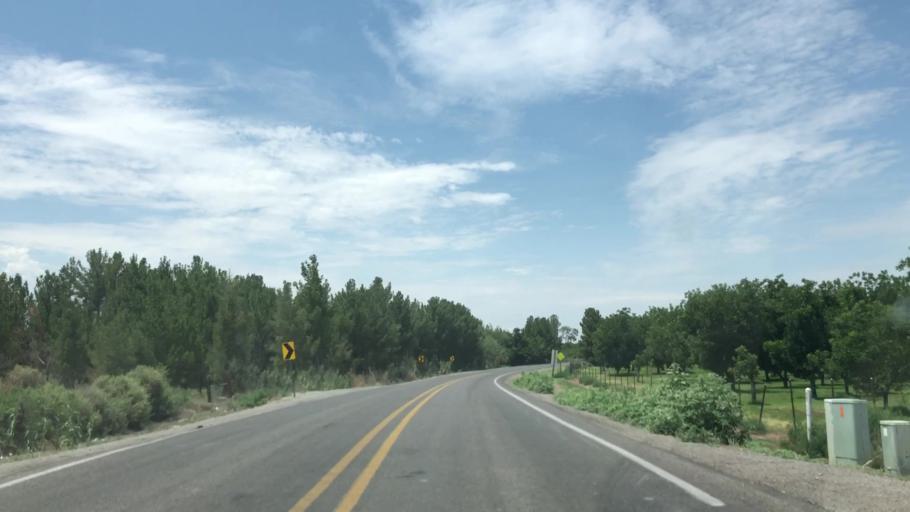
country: US
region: New Mexico
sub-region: Dona Ana County
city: Vado
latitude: 32.1130
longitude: -106.6698
